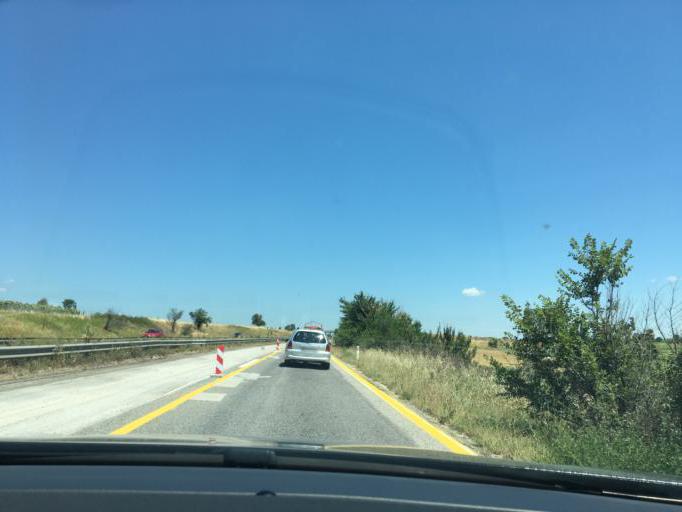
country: MK
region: Kumanovo
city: Romanovce
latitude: 42.0877
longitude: 21.7022
